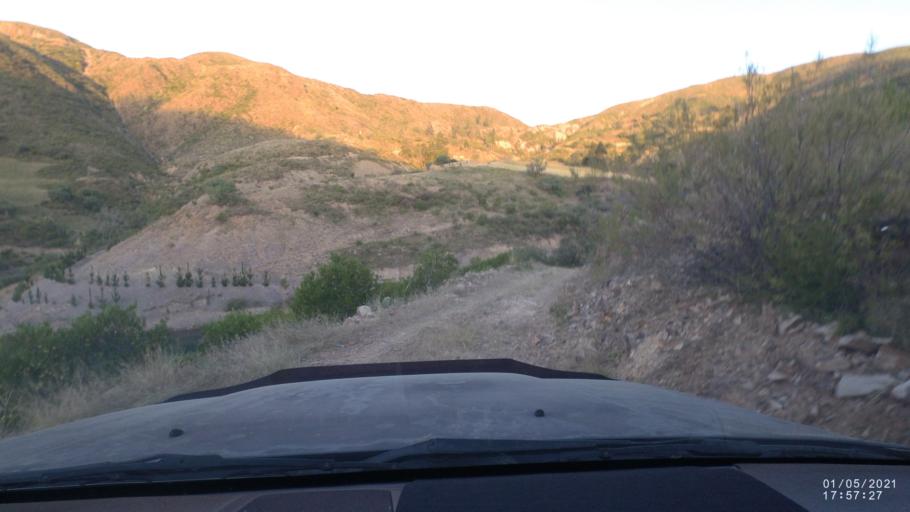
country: BO
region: Cochabamba
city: Capinota
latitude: -17.6858
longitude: -66.1691
